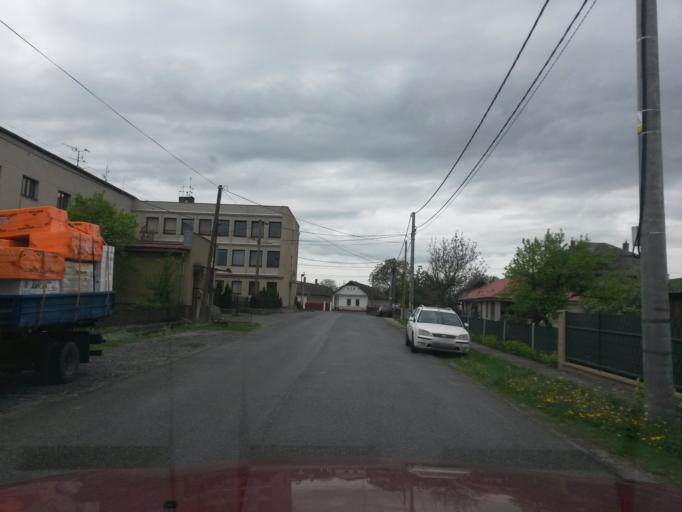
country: HU
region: Borsod-Abauj-Zemplen
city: Gonc
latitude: 48.5356
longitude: 21.1890
